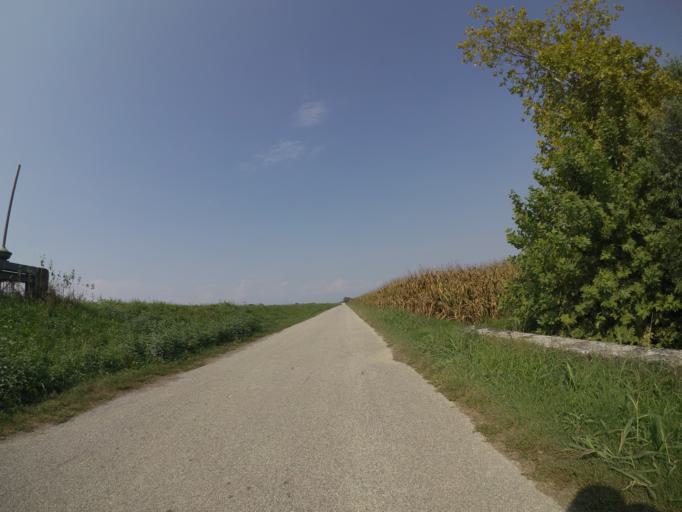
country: IT
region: Friuli Venezia Giulia
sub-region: Provincia di Udine
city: Camino al Tagliamento
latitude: 45.9214
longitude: 12.9254
